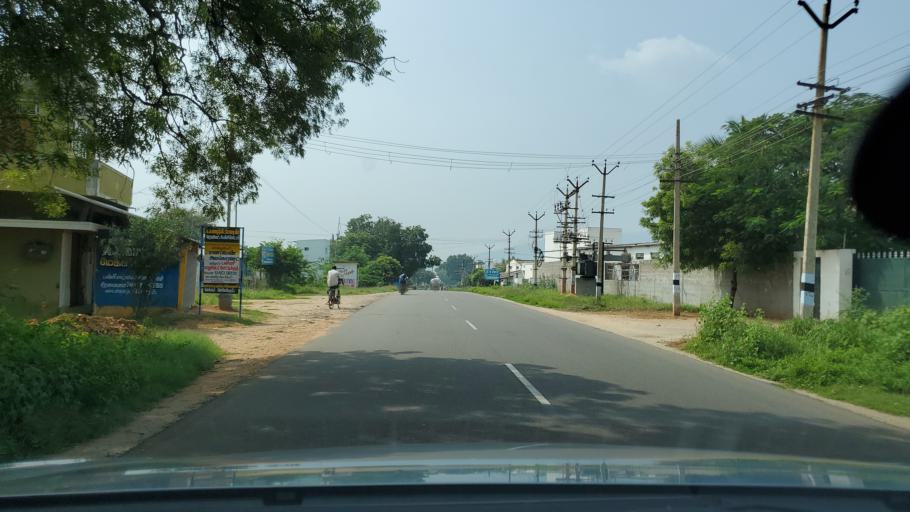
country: IN
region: Tamil Nadu
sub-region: Erode
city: Chennimalai
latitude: 11.1822
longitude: 77.6084
